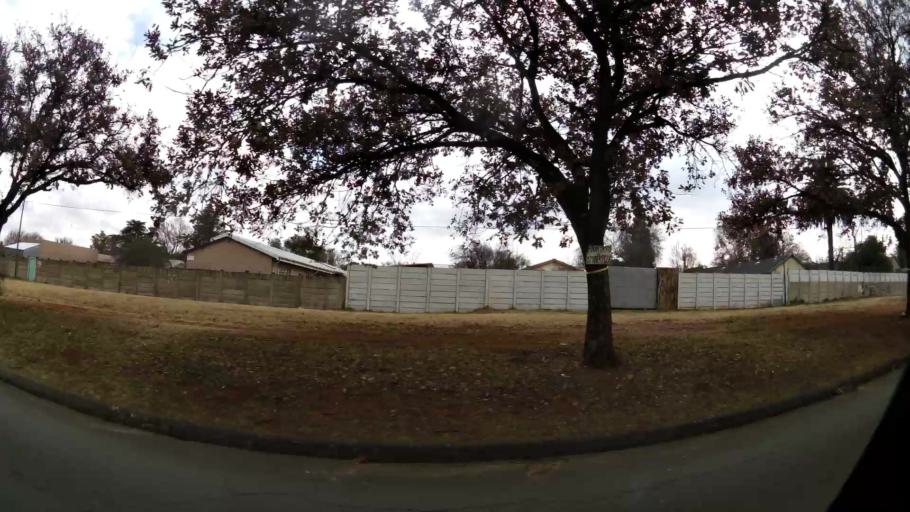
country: ZA
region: Gauteng
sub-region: Sedibeng District Municipality
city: Vanderbijlpark
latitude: -26.7303
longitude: 27.8374
